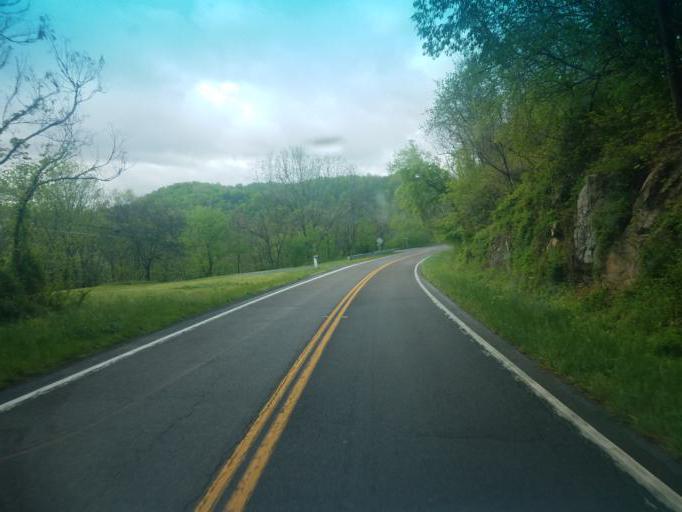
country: US
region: Virginia
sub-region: Washington County
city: Emory
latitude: 36.6696
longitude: -81.8029
